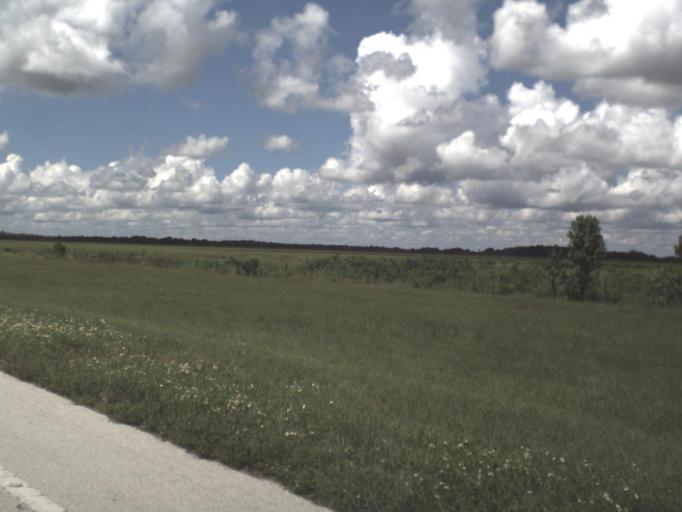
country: US
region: Florida
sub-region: DeSoto County
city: Southeast Arcadia
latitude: 27.2094
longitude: -81.7330
